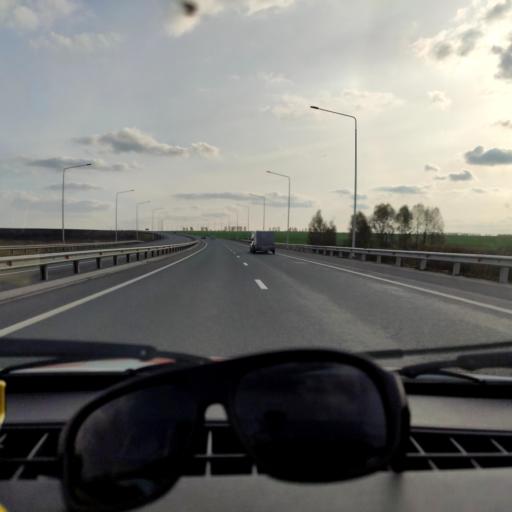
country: RU
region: Bashkortostan
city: Tolbazy
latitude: 54.3060
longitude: 55.8811
